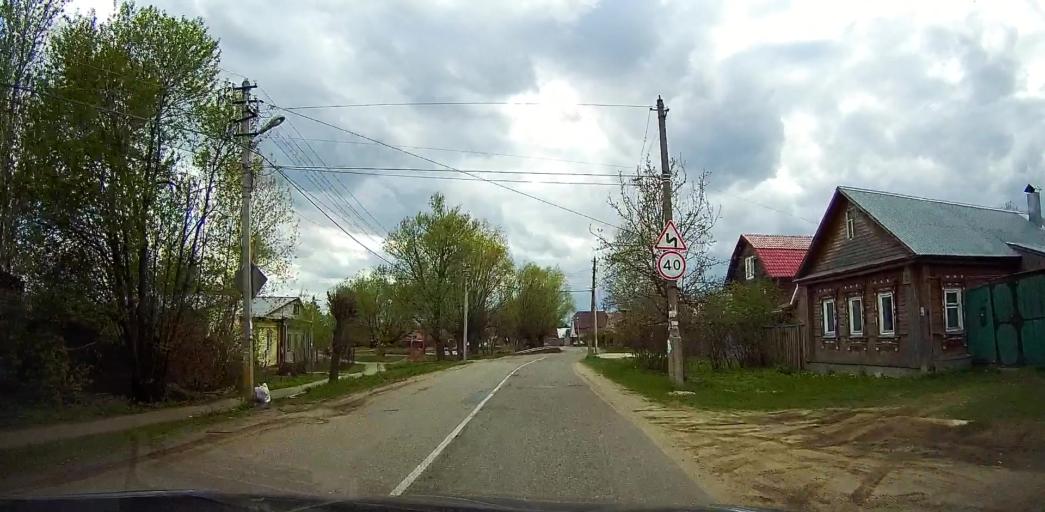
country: RU
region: Moskovskaya
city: Pavlovskiy Posad
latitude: 55.7792
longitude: 38.6419
